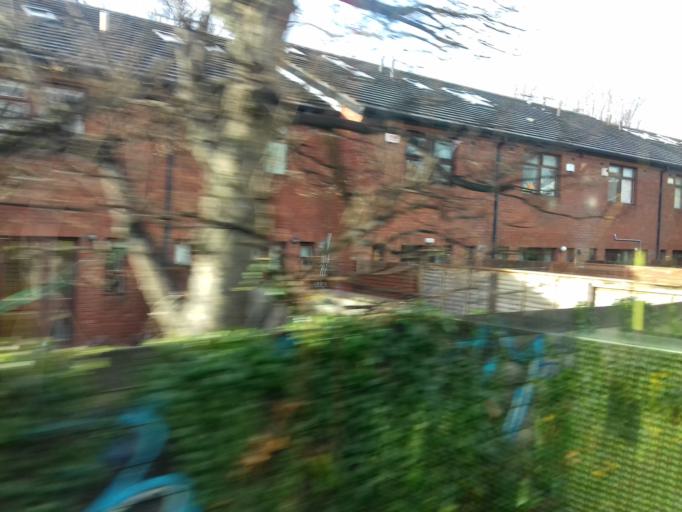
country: IE
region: Leinster
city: Sandymount
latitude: 53.3272
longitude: -6.2202
